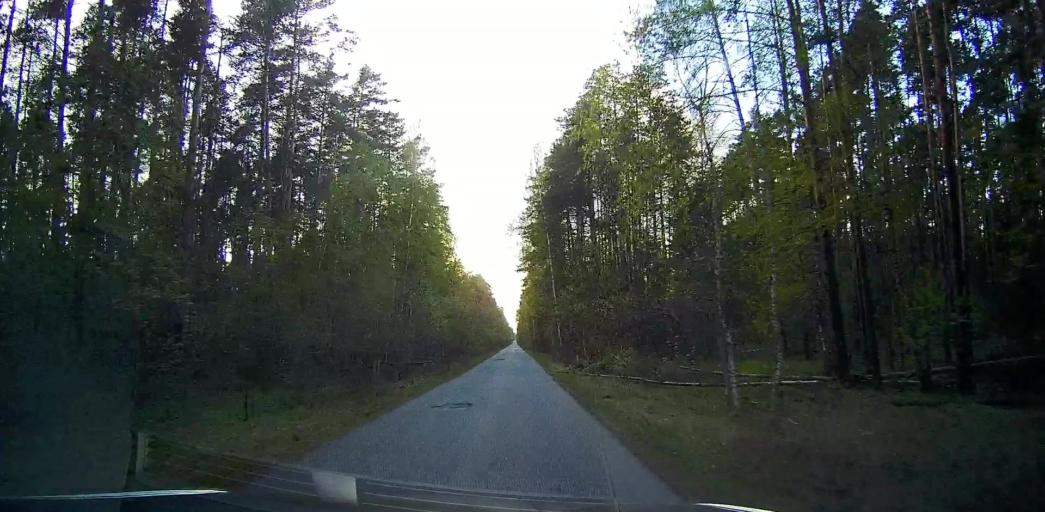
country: RU
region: Moskovskaya
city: Malyshevo
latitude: 55.5462
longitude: 38.3724
